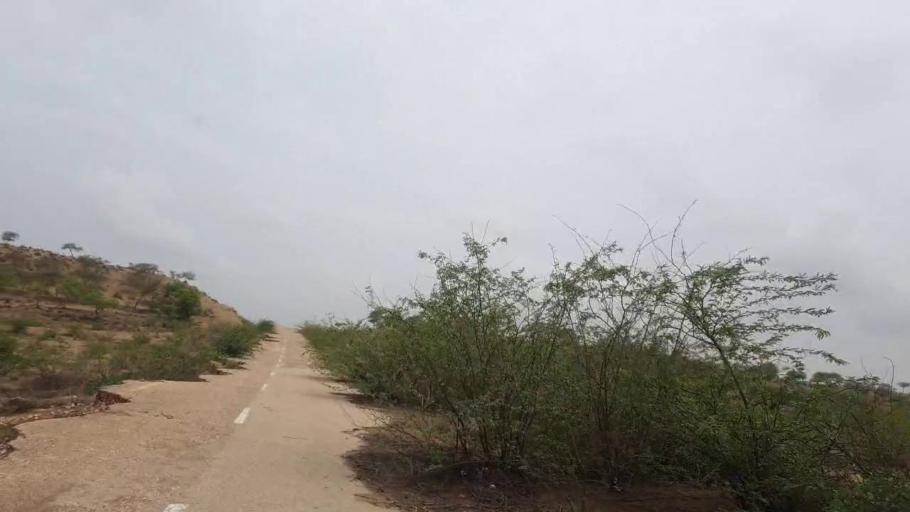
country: PK
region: Sindh
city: Naukot
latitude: 24.6303
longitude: 69.3553
